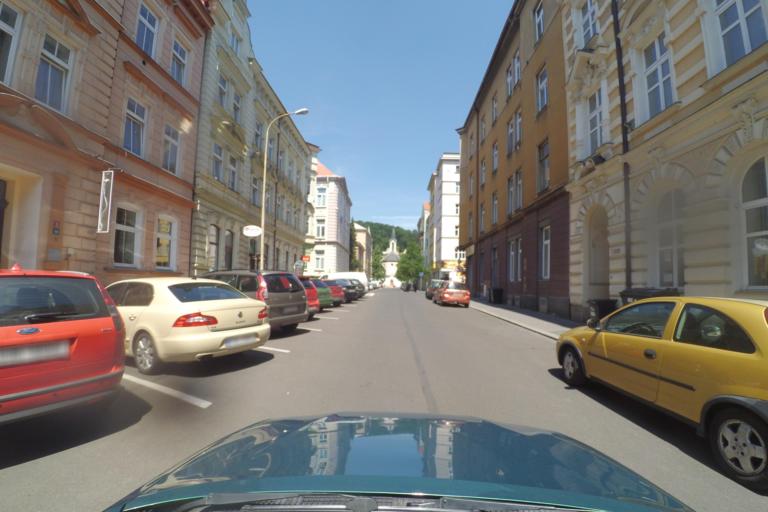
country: CZ
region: Ustecky
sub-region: Okres Decin
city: Decin
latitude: 50.7732
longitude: 14.1976
